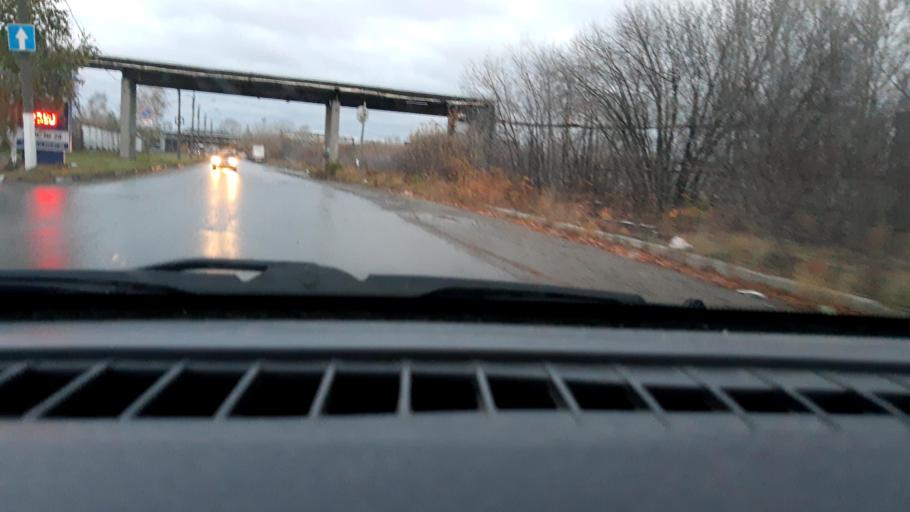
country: RU
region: Nizjnij Novgorod
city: Nizhniy Novgorod
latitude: 56.2393
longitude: 43.9065
